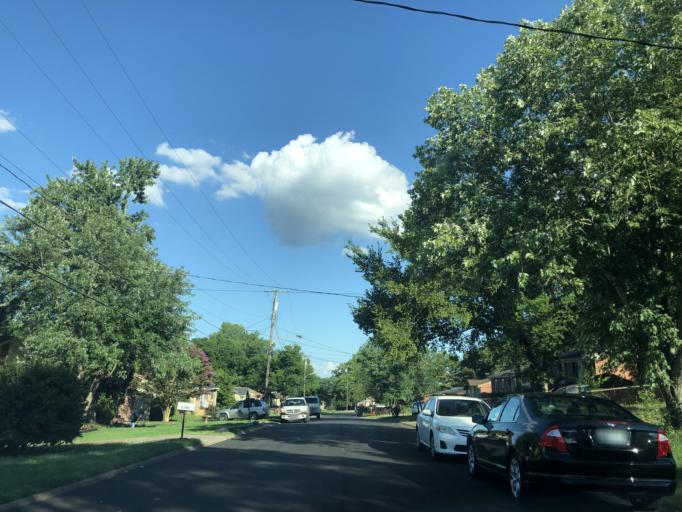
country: US
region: Tennessee
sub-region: Davidson County
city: Nashville
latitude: 36.1867
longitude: -86.8450
